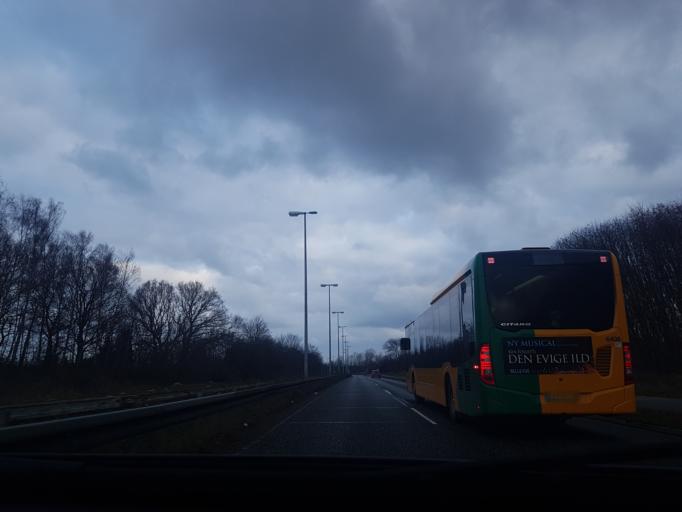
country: DK
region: Capital Region
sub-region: Brondby Kommune
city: Brondbyvester
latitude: 55.6315
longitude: 12.3958
